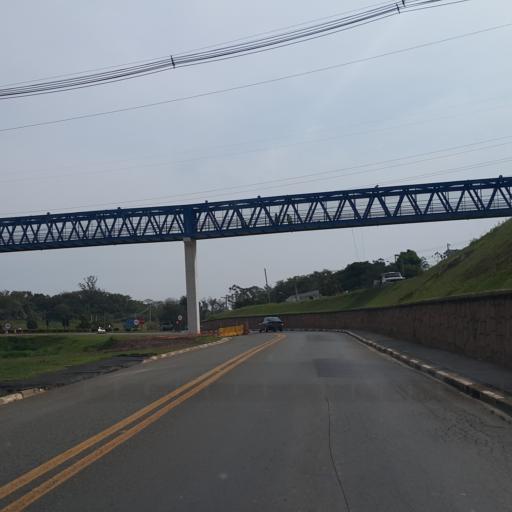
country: BR
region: Sao Paulo
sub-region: Louveira
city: Louveira
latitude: -23.0898
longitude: -46.9510
